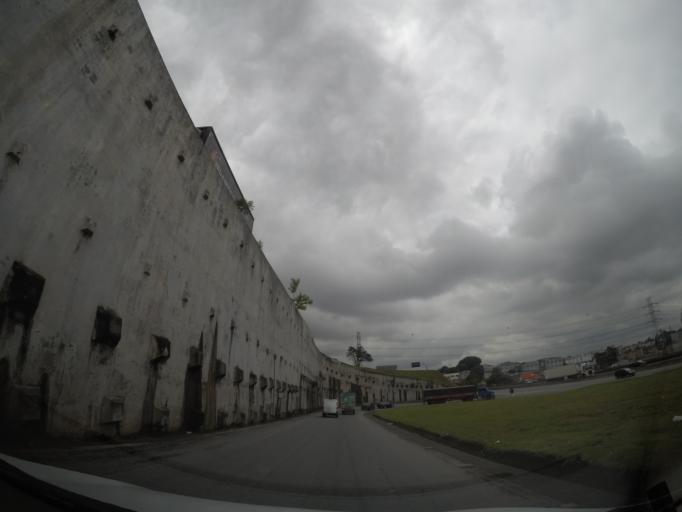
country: BR
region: Sao Paulo
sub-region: Guarulhos
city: Guarulhos
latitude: -23.4539
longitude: -46.4728
